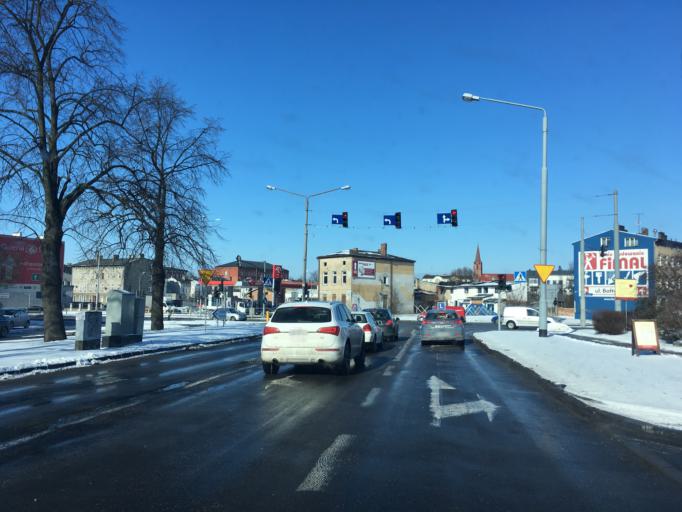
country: PL
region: Pomeranian Voivodeship
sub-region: Slupsk
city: Slupsk
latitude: 54.4644
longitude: 17.0416
